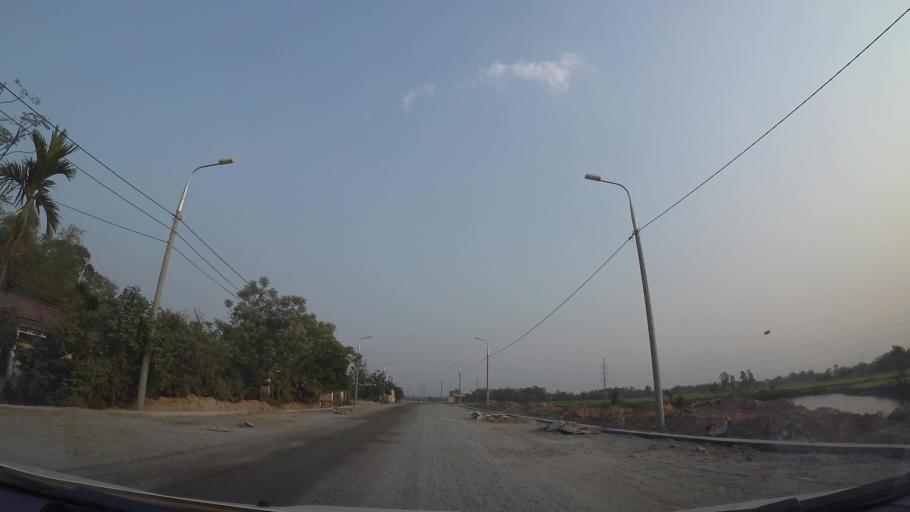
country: VN
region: Da Nang
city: Ngu Hanh Son
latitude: 15.9591
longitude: 108.2330
